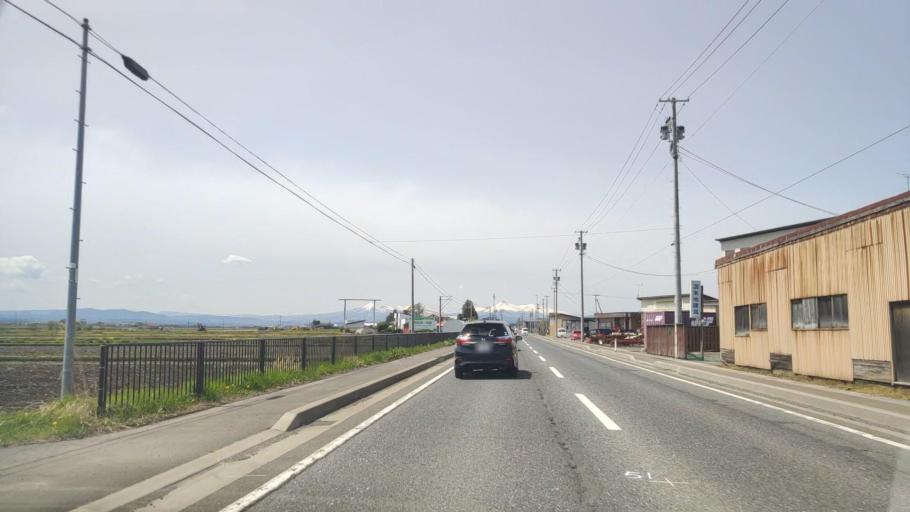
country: JP
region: Aomori
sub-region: Misawa Shi
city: Inuotose
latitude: 40.6098
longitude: 141.2806
